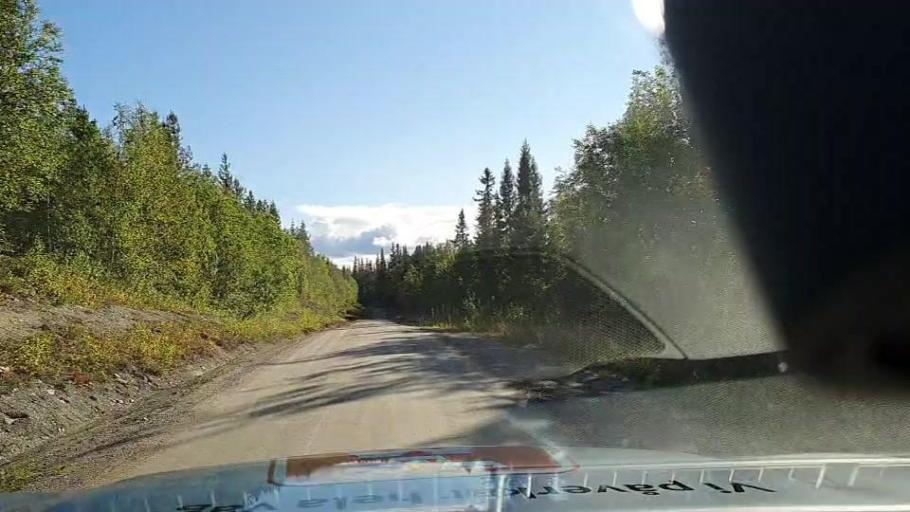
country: SE
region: Jaemtland
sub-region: Stroemsunds Kommun
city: Stroemsund
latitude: 64.5496
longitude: 15.0888
